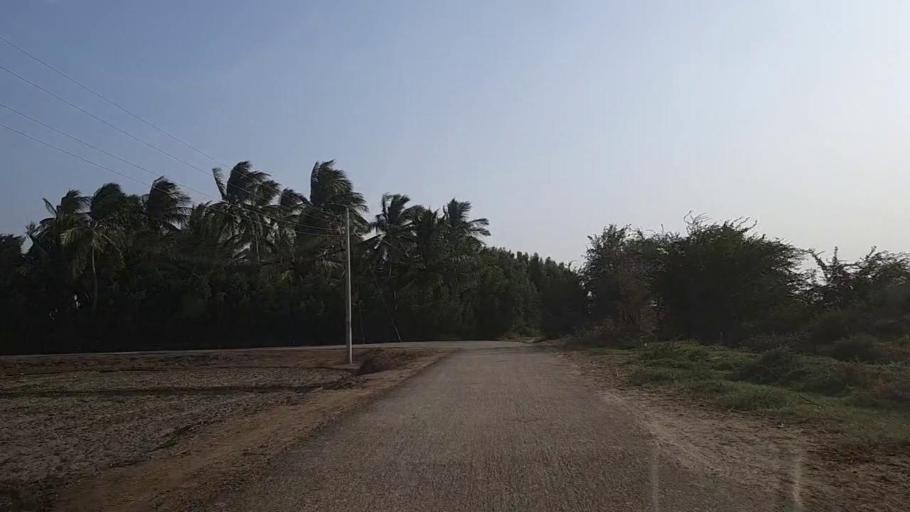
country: PK
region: Sindh
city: Keti Bandar
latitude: 24.1643
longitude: 67.6280
